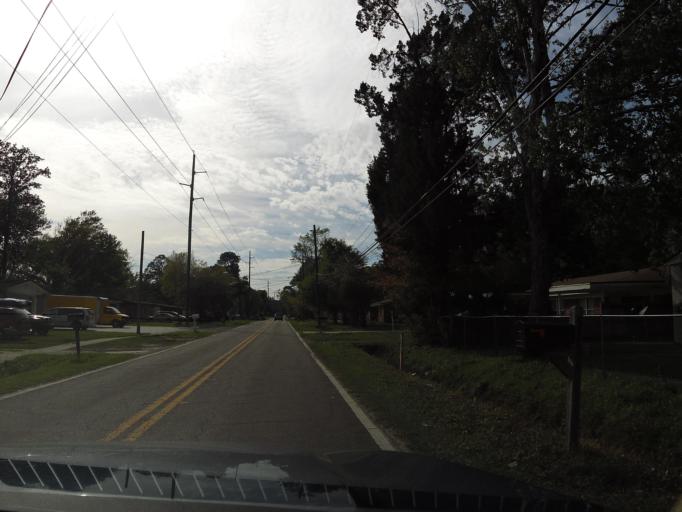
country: US
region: Florida
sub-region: Duval County
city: Jacksonville
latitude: 30.3031
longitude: -81.7367
